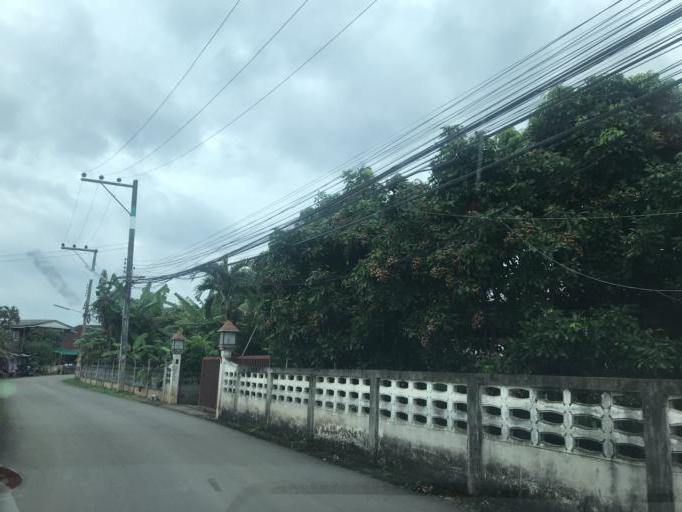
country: TH
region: Chiang Mai
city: Saraphi
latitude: 18.6945
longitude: 99.0251
